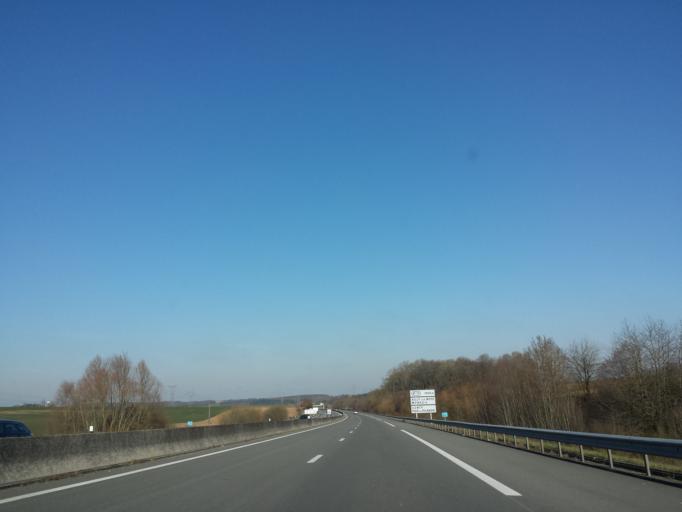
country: FR
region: Picardie
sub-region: Departement de la Somme
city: Conty
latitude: 49.7234
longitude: 2.2397
